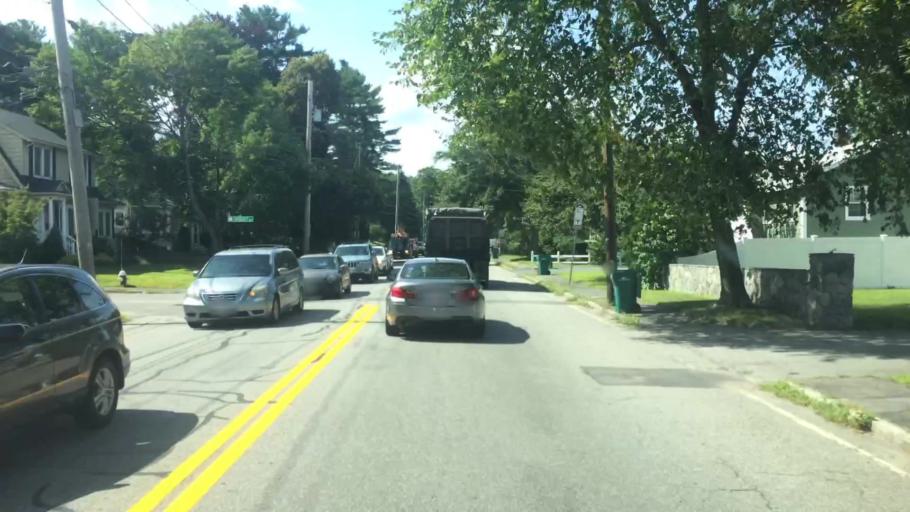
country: US
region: Massachusetts
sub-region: Essex County
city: South Peabody
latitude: 42.5100
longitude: -70.9893
